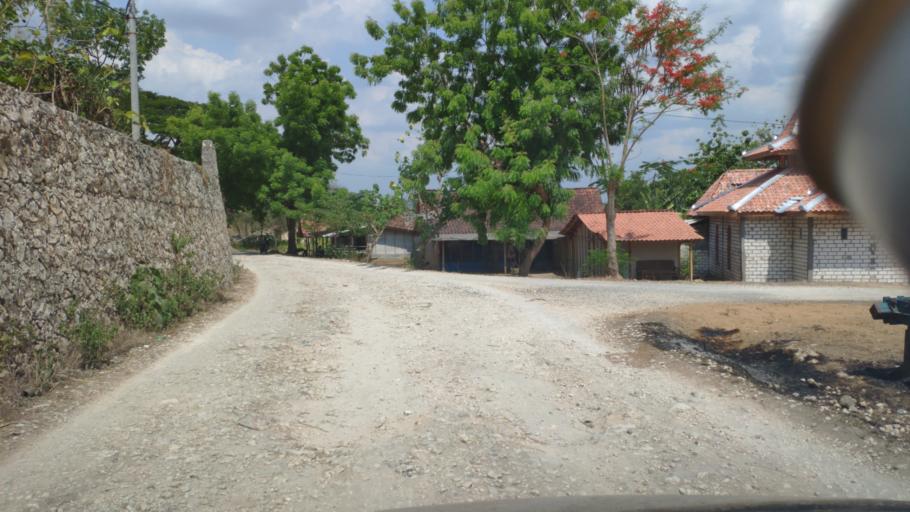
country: ID
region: Central Java
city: Pelem
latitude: -6.9891
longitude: 111.2033
